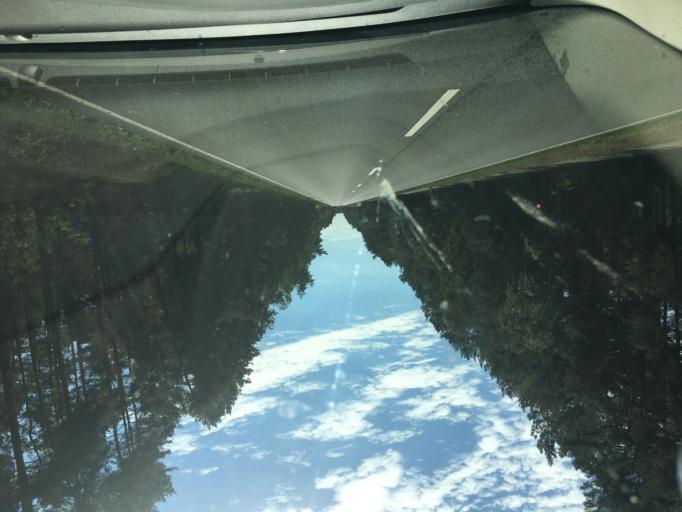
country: DE
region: Saxony-Anhalt
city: Seehausen
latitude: 52.8516
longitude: 11.7319
